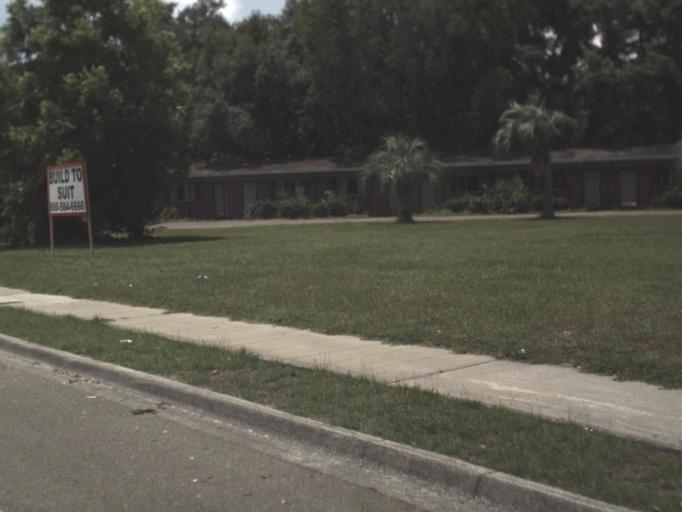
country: US
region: Florida
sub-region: Taylor County
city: Perry
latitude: 30.0962
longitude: -83.5813
